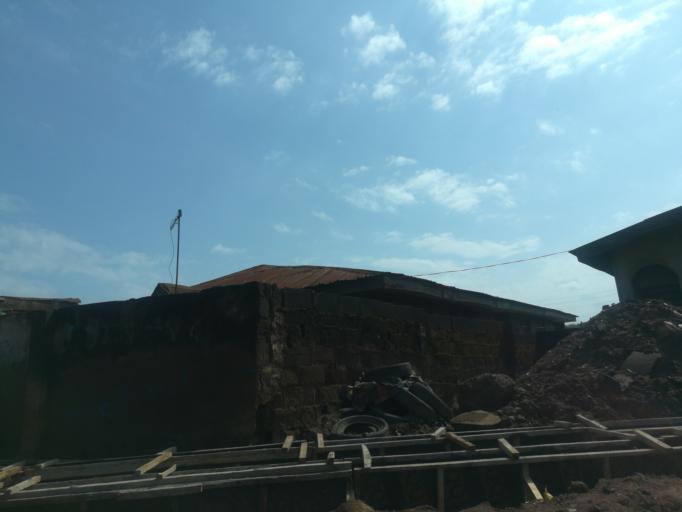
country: NG
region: Oyo
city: Egbeda
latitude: 7.4160
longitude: 3.9785
